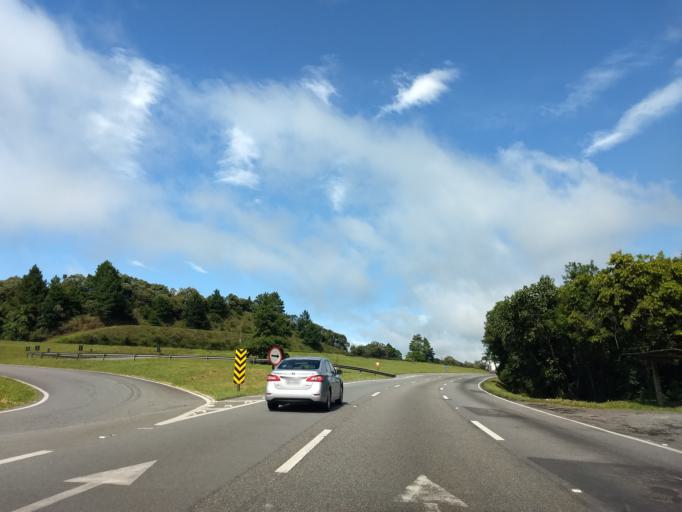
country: BR
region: Parana
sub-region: Sao Jose Dos Pinhais
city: Sao Jose dos Pinhais
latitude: -25.8407
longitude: -49.0430
